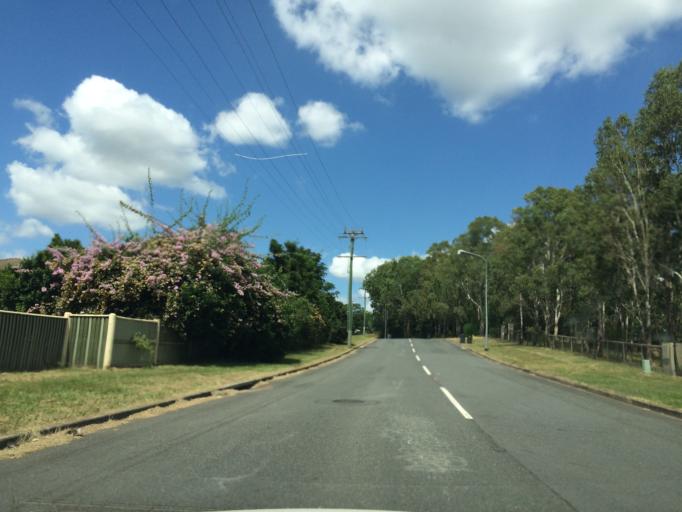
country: AU
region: Queensland
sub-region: Brisbane
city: Kenmore Hills
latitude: -27.5079
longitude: 152.9150
